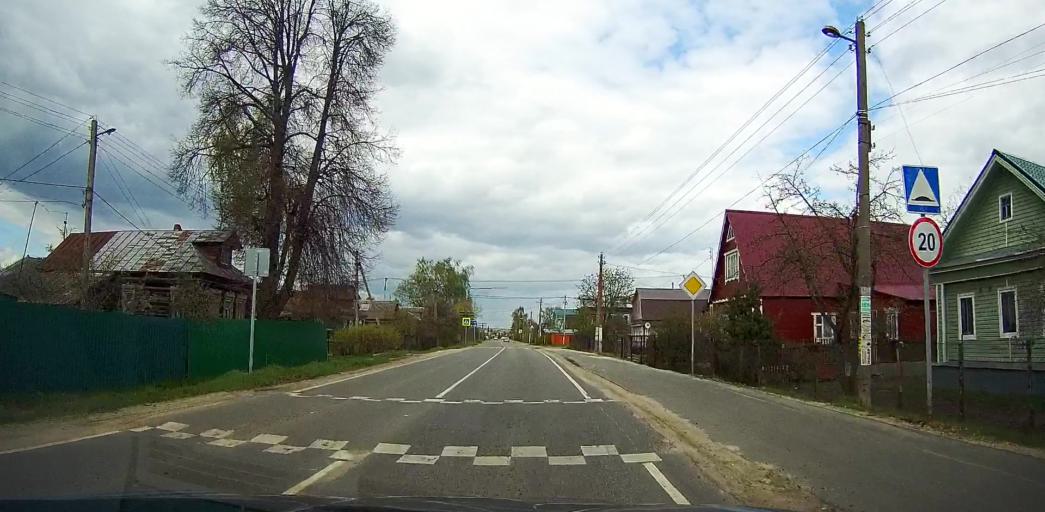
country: RU
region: Moskovskaya
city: Ashitkovo
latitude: 55.4460
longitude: 38.5915
